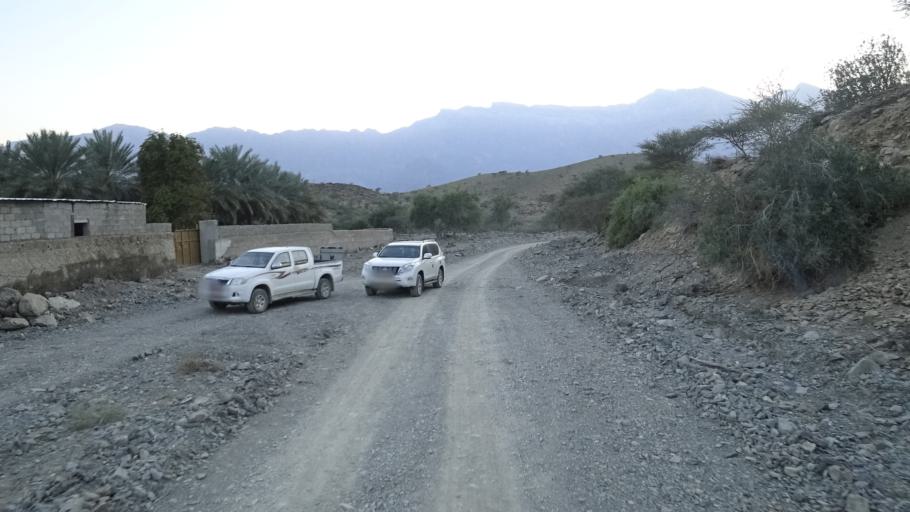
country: OM
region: Al Batinah
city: Rustaq
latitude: 23.2797
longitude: 57.3564
